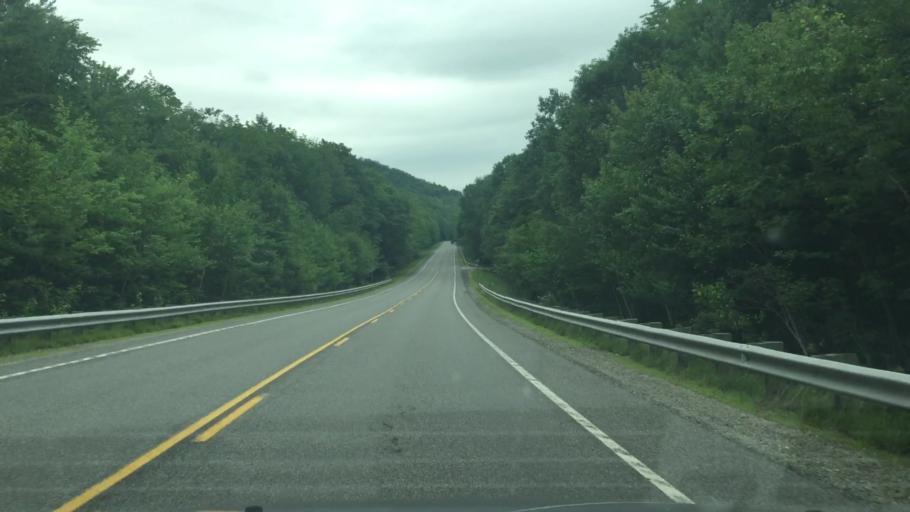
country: US
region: New Hampshire
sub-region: Carroll County
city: North Conway
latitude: 44.0890
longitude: -71.3532
